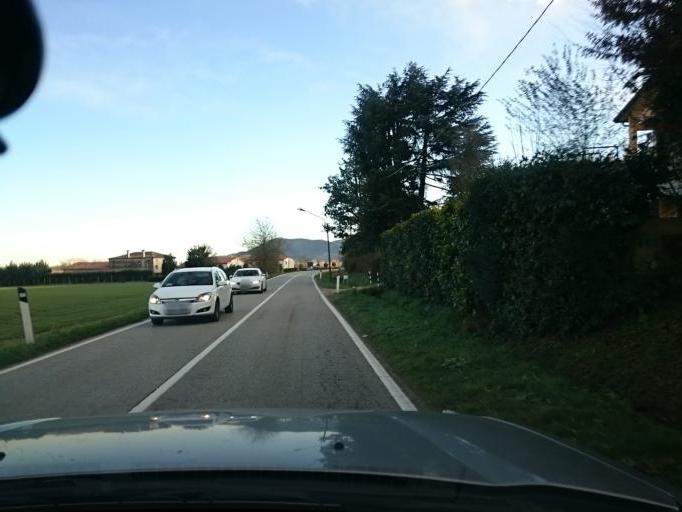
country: IT
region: Veneto
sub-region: Provincia di Padova
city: Torreglia
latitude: 45.3488
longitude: 11.7367
